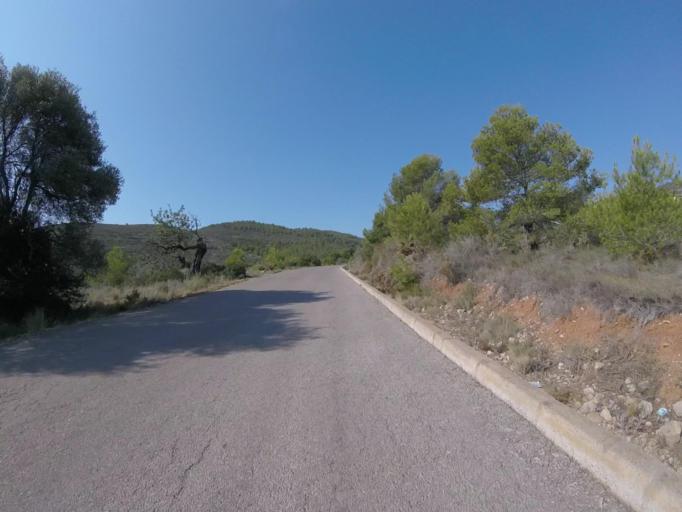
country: ES
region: Valencia
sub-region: Provincia de Castello
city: Peniscola
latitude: 40.3336
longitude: 0.3675
